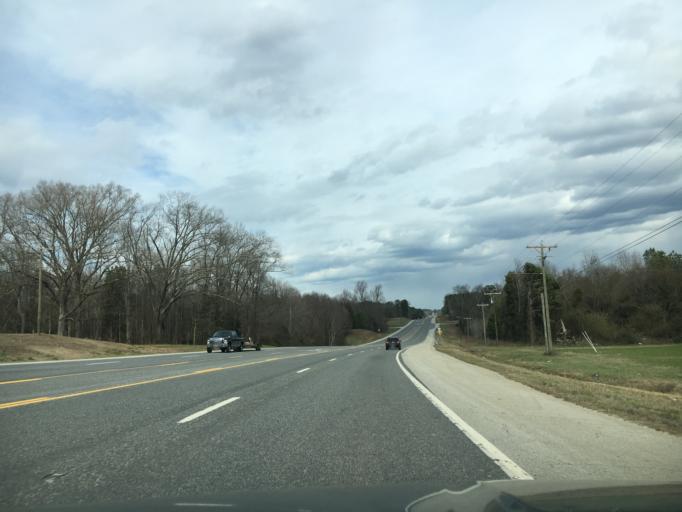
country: US
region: Virginia
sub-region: Mecklenburg County
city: South Hill
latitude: 36.6862
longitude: -78.2044
